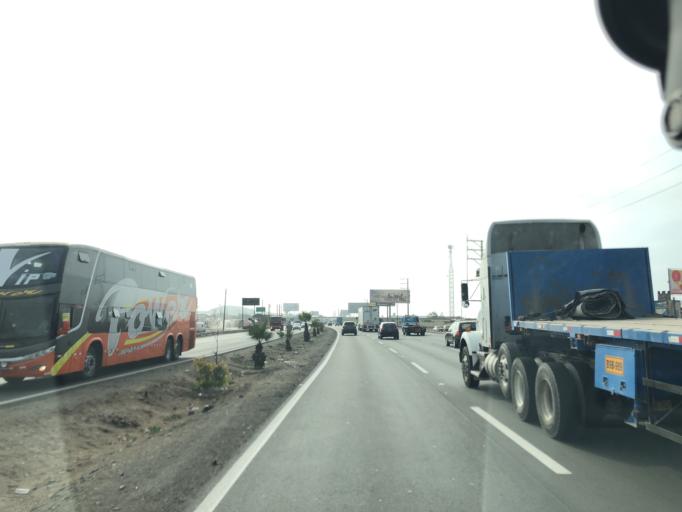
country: PE
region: Lima
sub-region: Lima
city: Punta Hermosa
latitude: -12.2526
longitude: -76.9278
